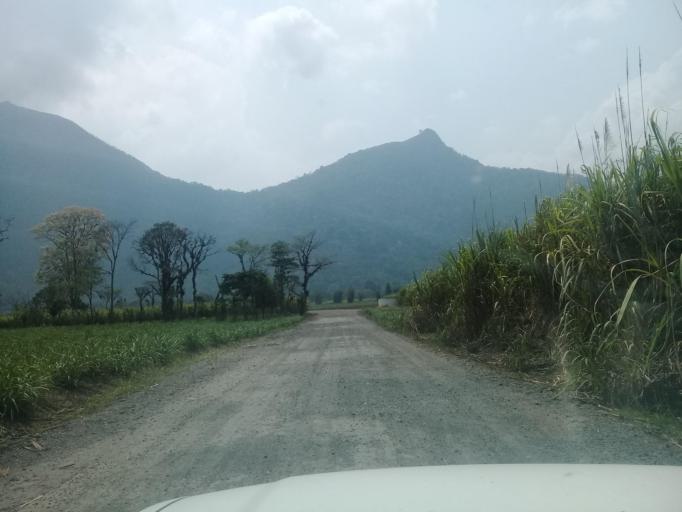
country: MX
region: Veracruz
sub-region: Ixtaczoquitlan
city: Capoluca
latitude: 18.8134
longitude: -96.9921
